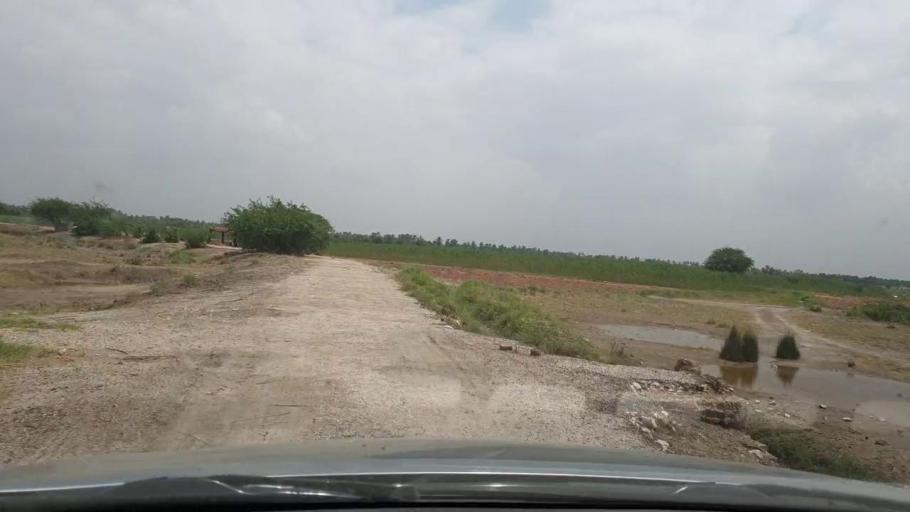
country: PK
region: Sindh
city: Kot Diji
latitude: 27.4277
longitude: 68.7593
